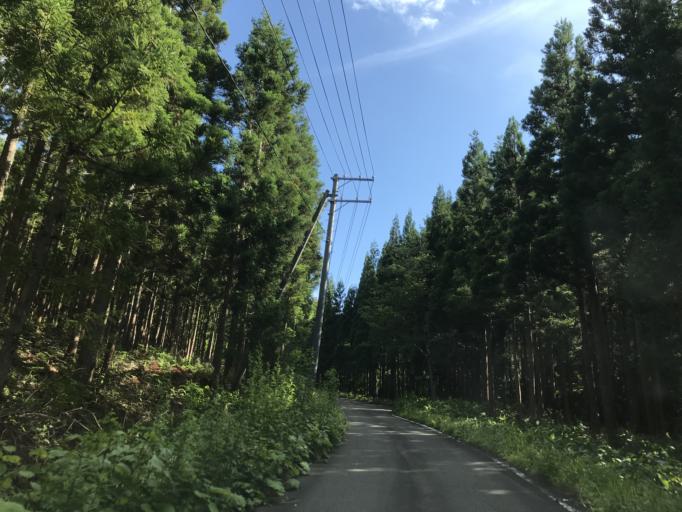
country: JP
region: Iwate
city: Ichinoseki
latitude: 38.8939
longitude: 140.9071
